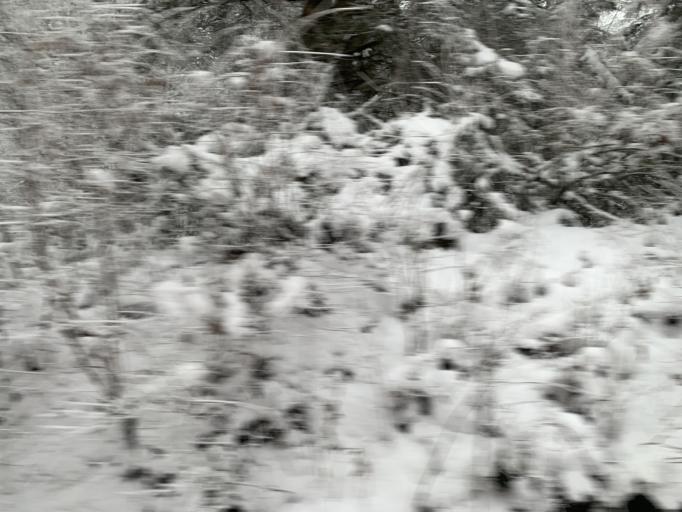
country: DE
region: Bavaria
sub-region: Upper Bavaria
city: Garmisch-Partenkirchen
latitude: 47.4833
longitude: 11.1430
